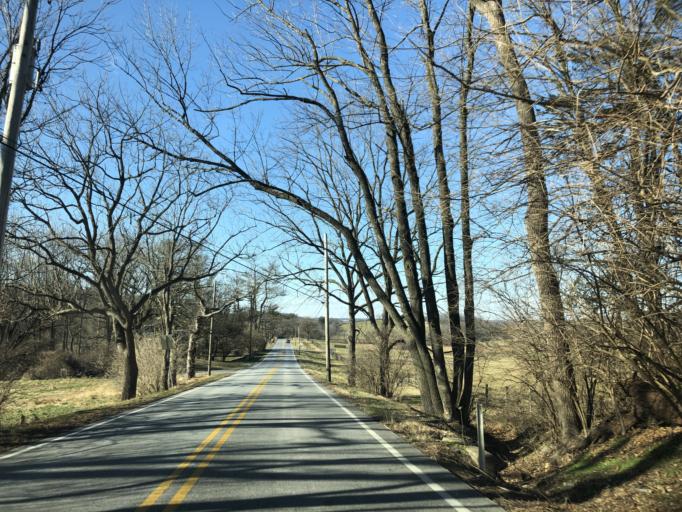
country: US
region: Pennsylvania
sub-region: Chester County
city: Upland
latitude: 39.9004
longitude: -75.7681
